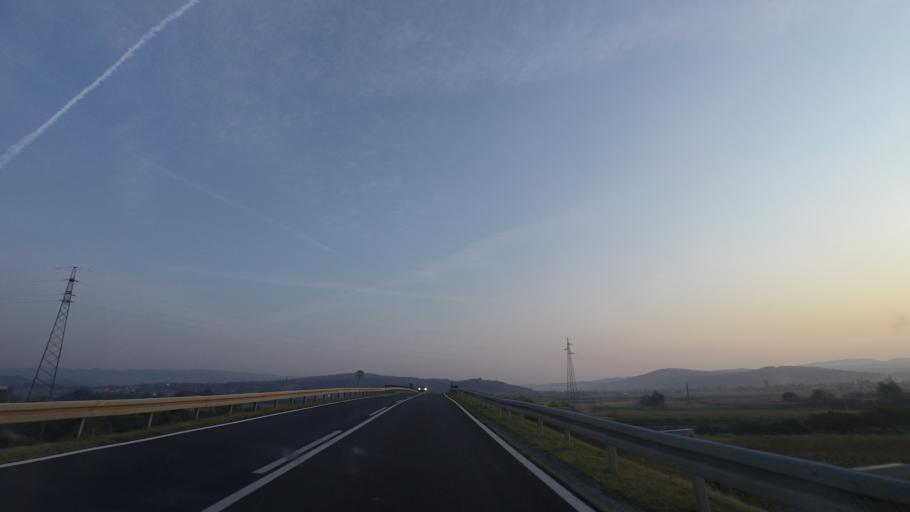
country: HR
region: Brodsko-Posavska
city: Nova Gradiska
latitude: 45.2461
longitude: 17.4082
